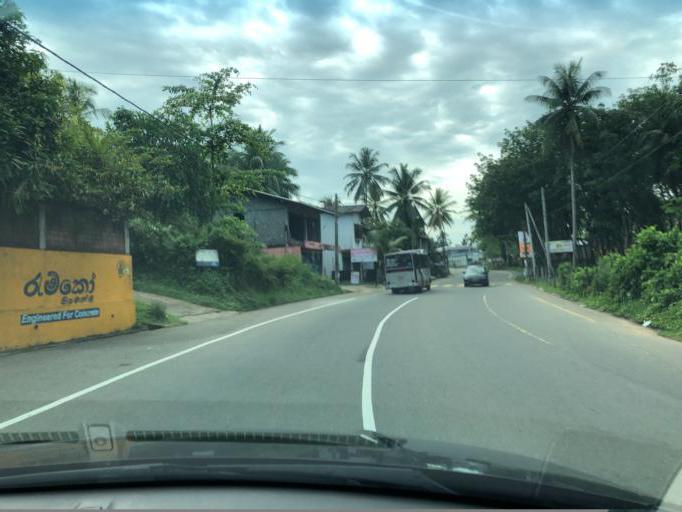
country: LK
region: Western
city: Kalutara
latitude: 6.5552
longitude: 80.0161
